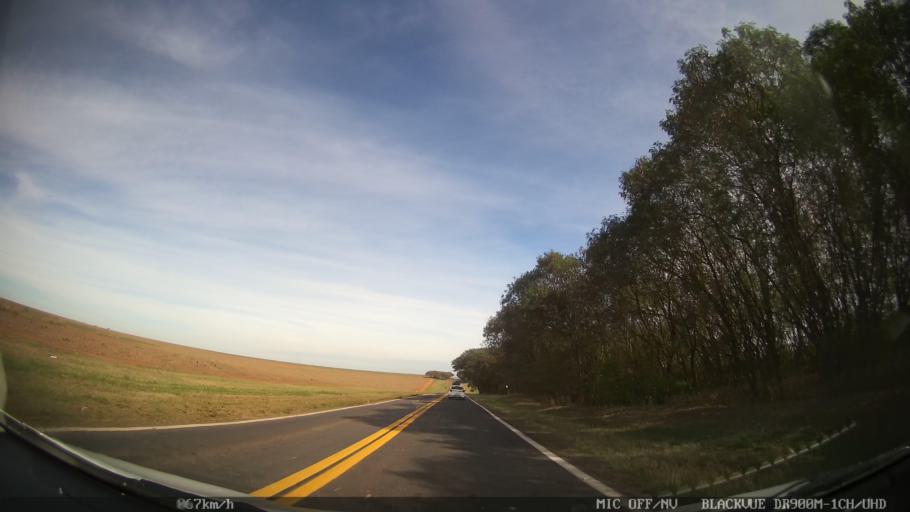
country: BR
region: Sao Paulo
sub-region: Rio Das Pedras
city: Rio das Pedras
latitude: -22.7952
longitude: -47.5915
